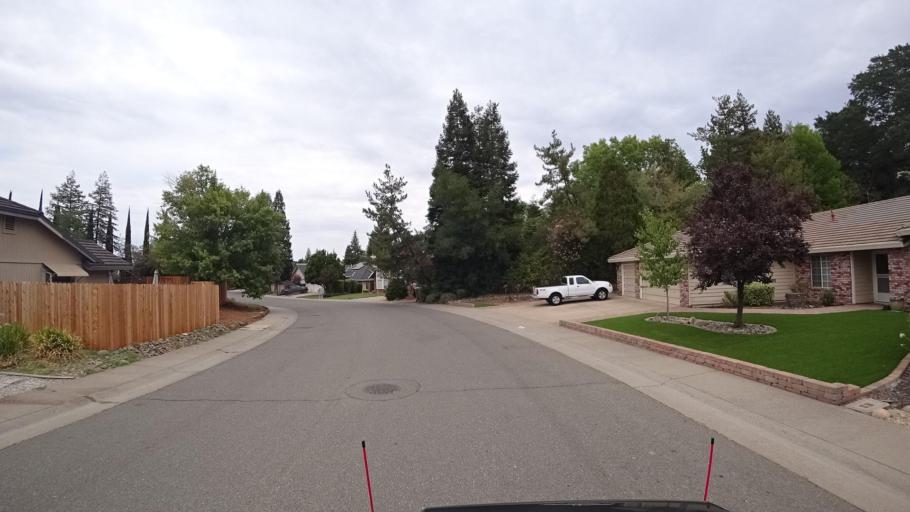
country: US
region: California
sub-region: Placer County
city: Rocklin
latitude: 38.7928
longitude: -121.2581
